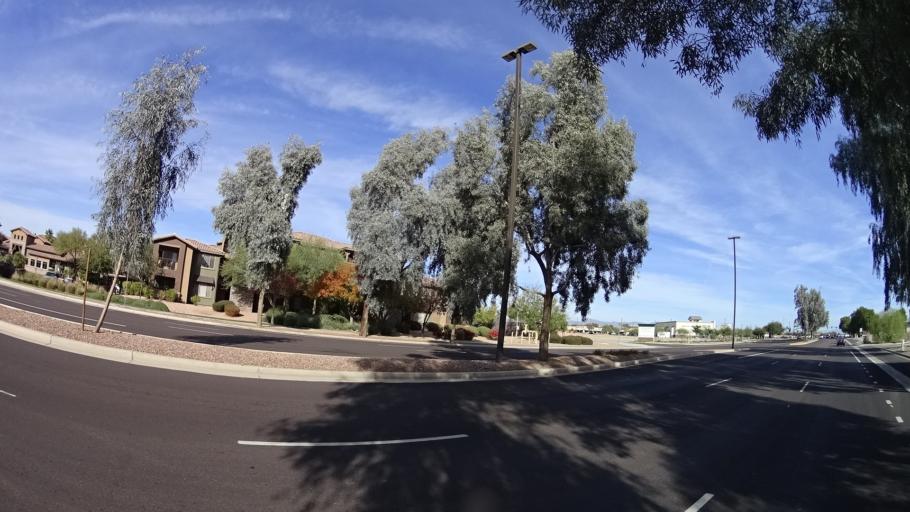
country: US
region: Arizona
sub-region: Maricopa County
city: Queen Creek
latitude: 33.2781
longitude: -111.6891
